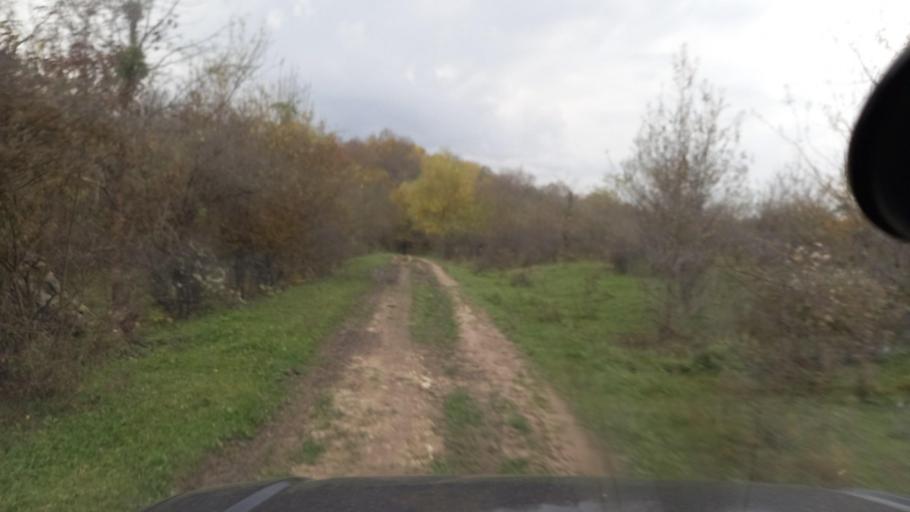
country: RU
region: Krasnodarskiy
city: Gubskaya
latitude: 44.2870
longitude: 40.5375
